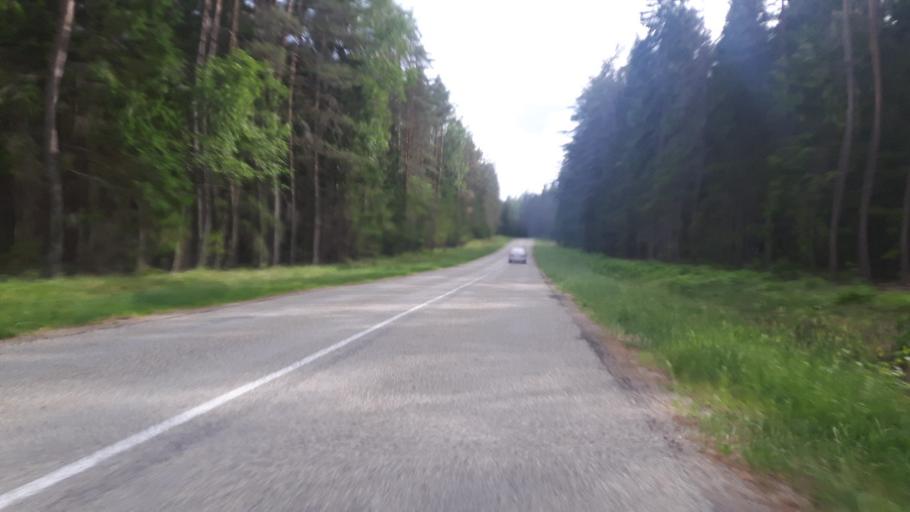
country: LV
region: Engure
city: Smarde
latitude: 57.0097
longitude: 23.3389
